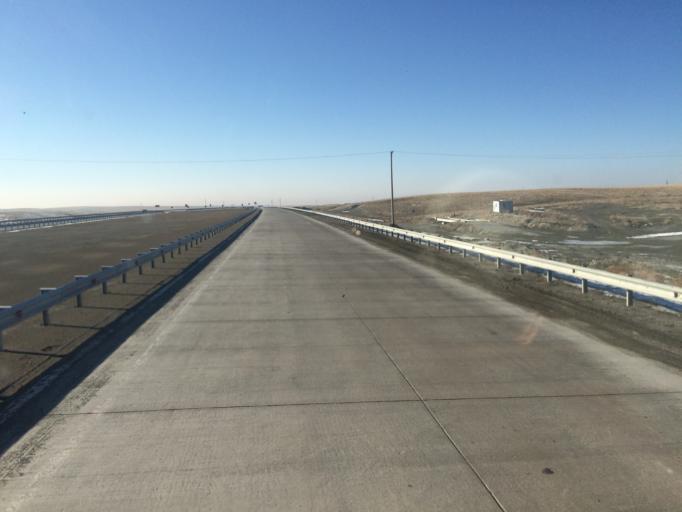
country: KZ
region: Zhambyl
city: Georgiyevka
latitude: 43.3547
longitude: 74.5679
